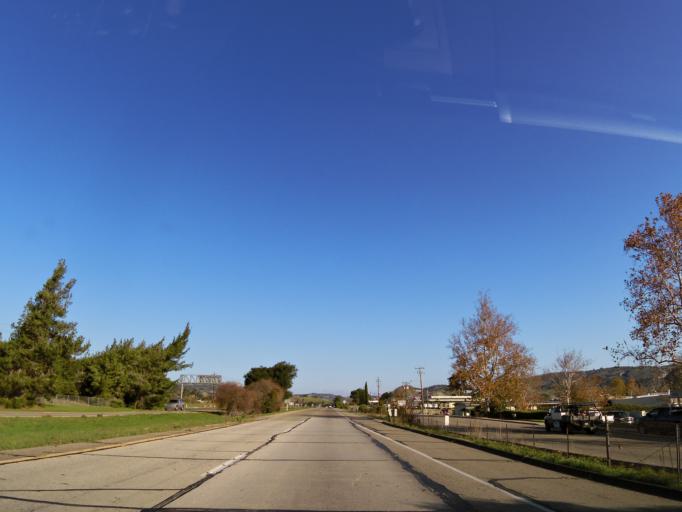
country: US
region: California
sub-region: Santa Barbara County
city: Buellton
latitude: 34.6223
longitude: -120.1892
